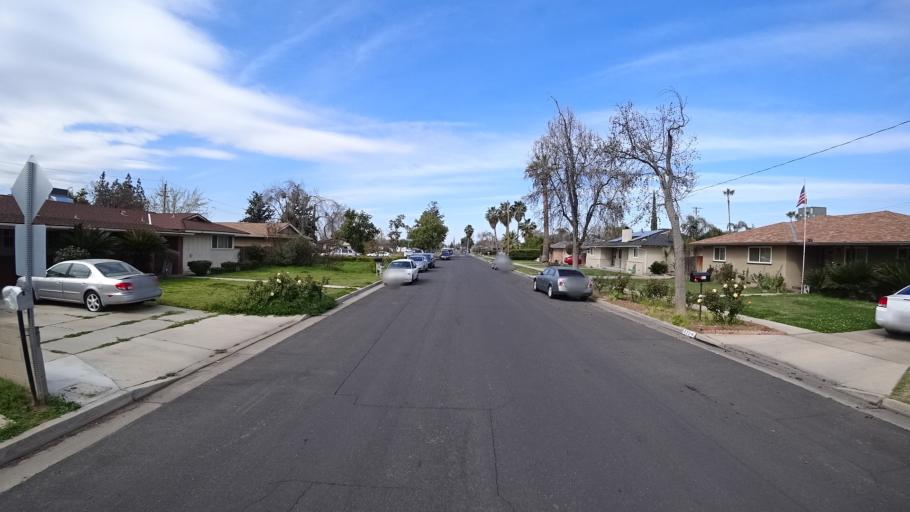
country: US
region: California
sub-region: Fresno County
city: Fresno
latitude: 36.8122
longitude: -119.7785
